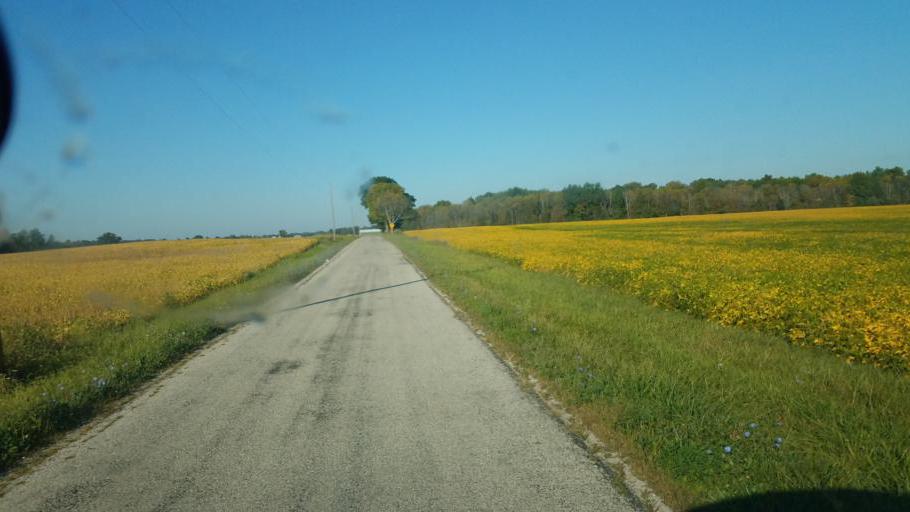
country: US
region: Ohio
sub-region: Marion County
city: Prospect
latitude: 40.5326
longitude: -83.2326
